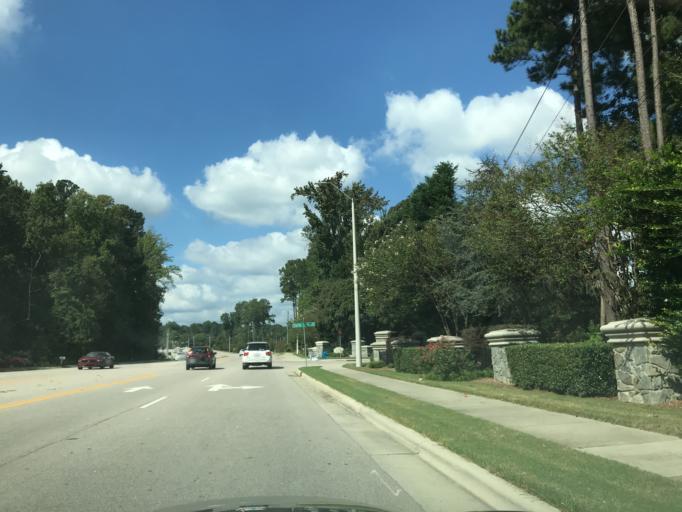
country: US
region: North Carolina
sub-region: Wake County
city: Wake Forest
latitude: 35.8892
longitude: -78.5560
